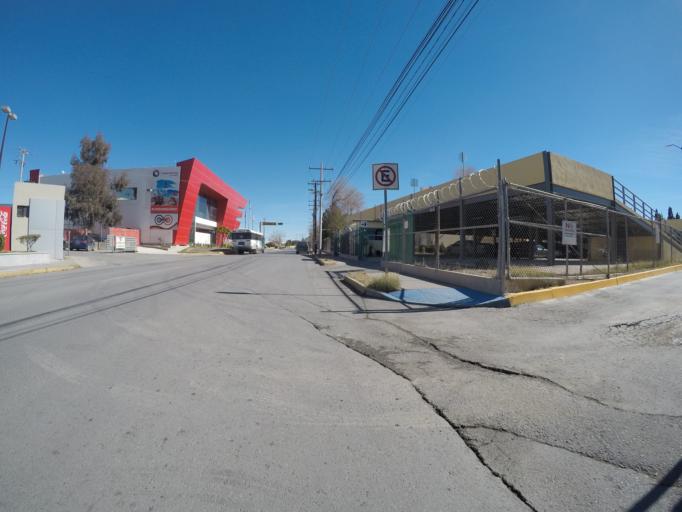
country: MX
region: Chihuahua
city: Ciudad Juarez
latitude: 31.7413
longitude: -106.4458
